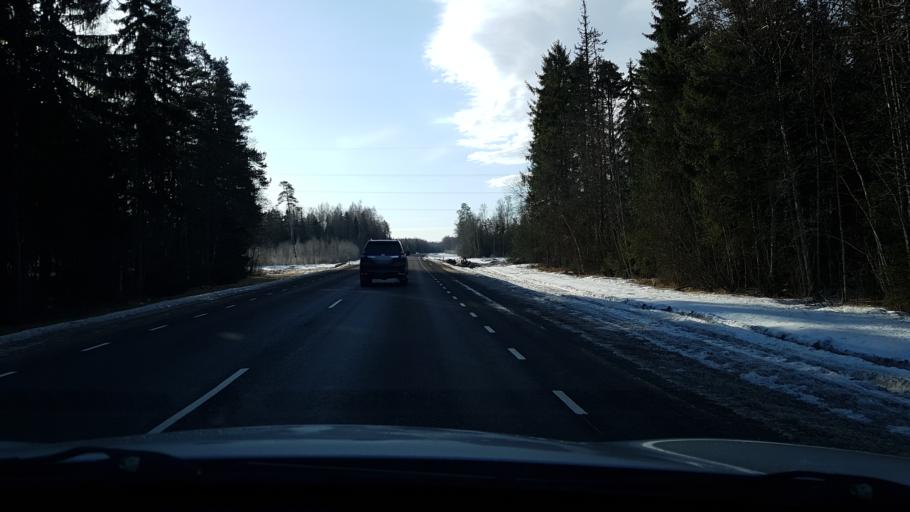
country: EE
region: Viljandimaa
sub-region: Vohma linn
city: Vohma
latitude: 58.6117
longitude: 25.5715
